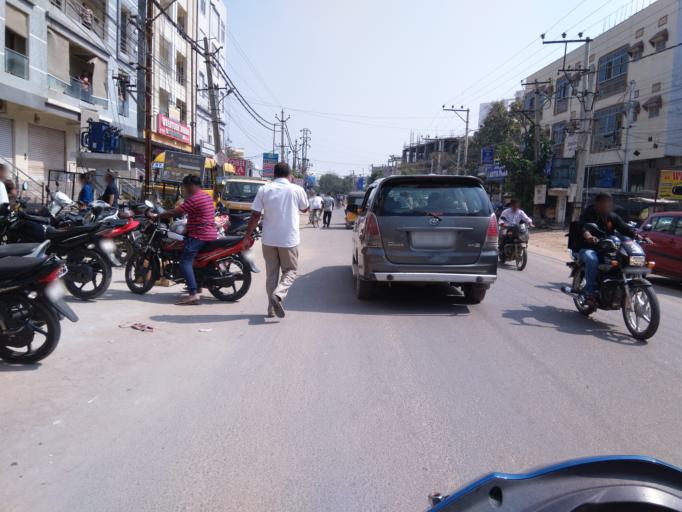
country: IN
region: Telangana
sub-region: Rangareddi
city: Kukatpalli
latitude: 17.4986
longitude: 78.4115
